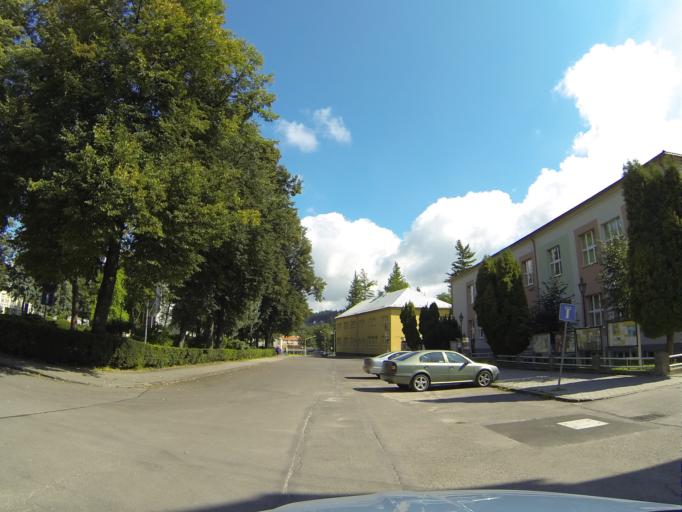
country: SK
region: Nitriansky
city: Handlova
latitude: 48.7279
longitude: 18.7605
